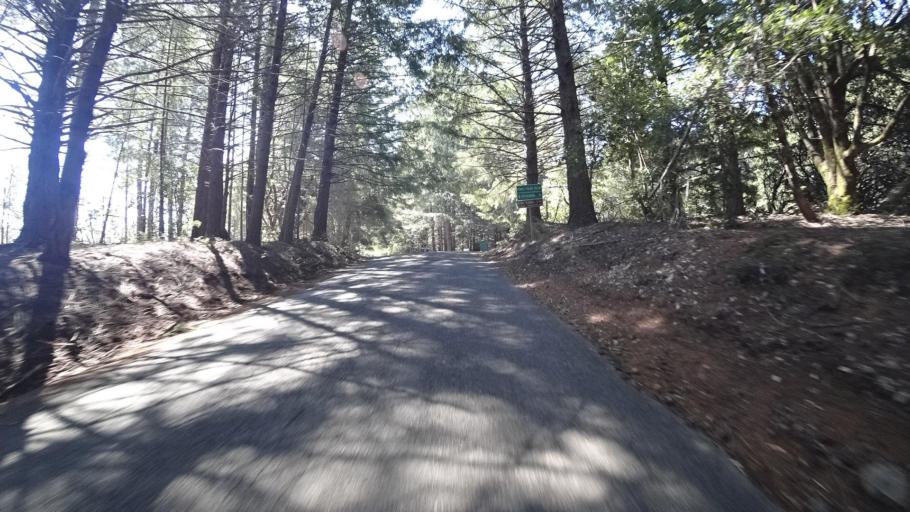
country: US
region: California
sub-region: Humboldt County
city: Redway
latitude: 40.1599
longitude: -124.0801
